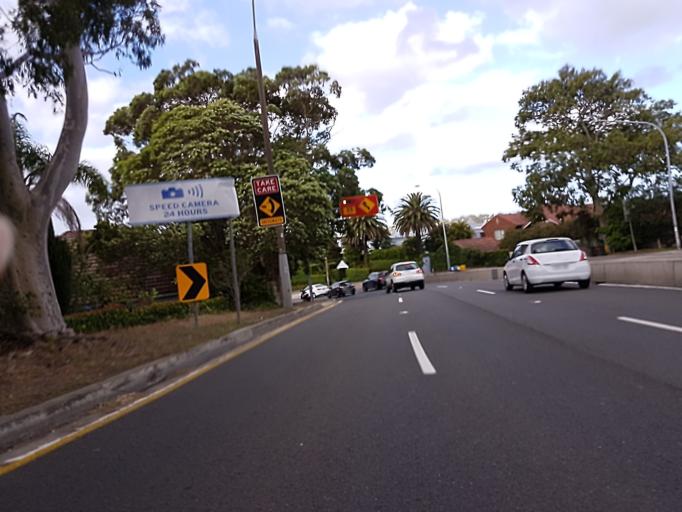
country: AU
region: New South Wales
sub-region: Manly Vale
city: Clontarf
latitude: -33.8128
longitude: 151.2442
